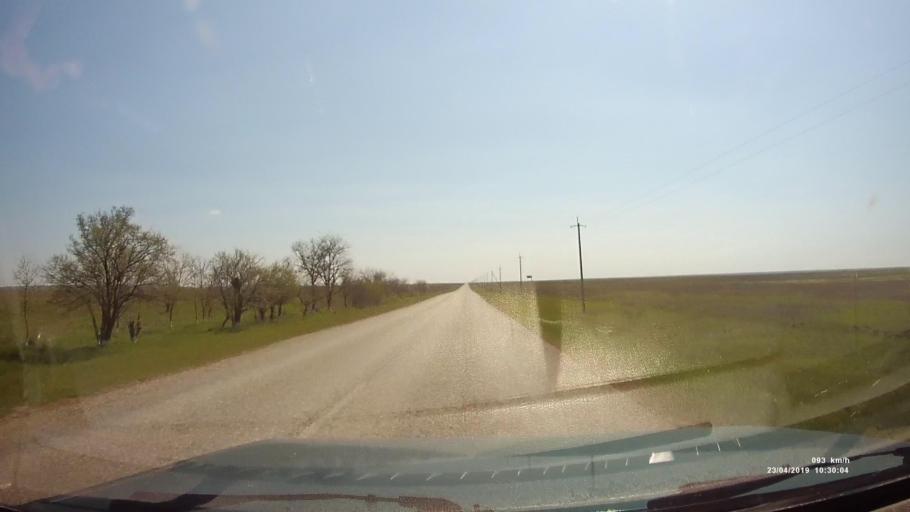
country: RU
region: Kalmykiya
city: Yashalta
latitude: 46.5945
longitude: 42.5377
